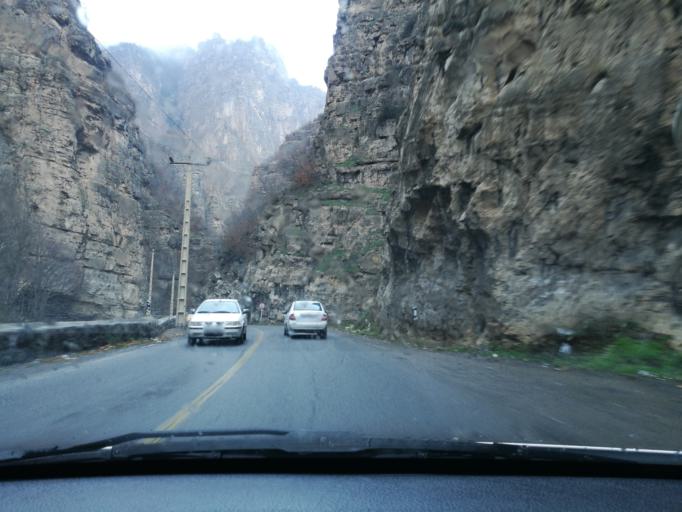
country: IR
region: Mazandaran
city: Chalus
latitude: 36.2700
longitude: 51.2488
